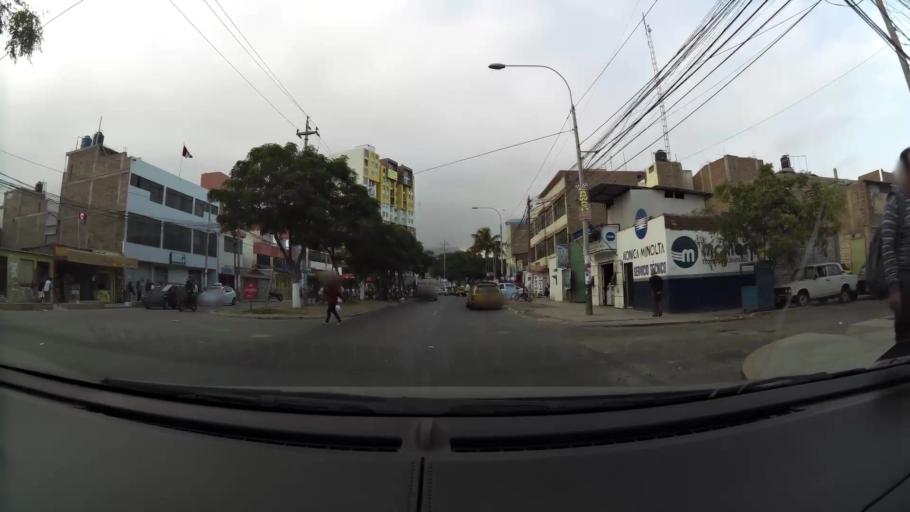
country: PE
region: La Libertad
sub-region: Provincia de Trujillo
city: La Esperanza
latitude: -8.0984
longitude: -79.0433
